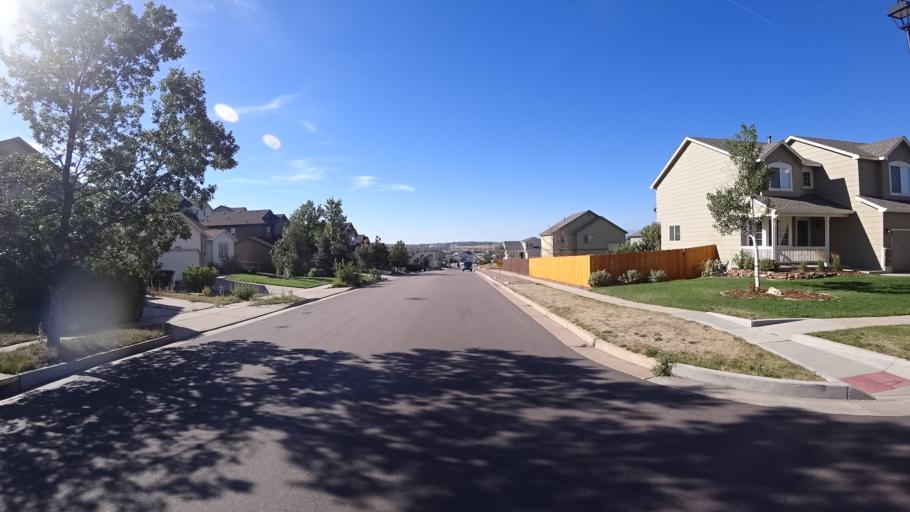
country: US
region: Colorado
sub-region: El Paso County
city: Black Forest
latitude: 38.9443
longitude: -104.7386
